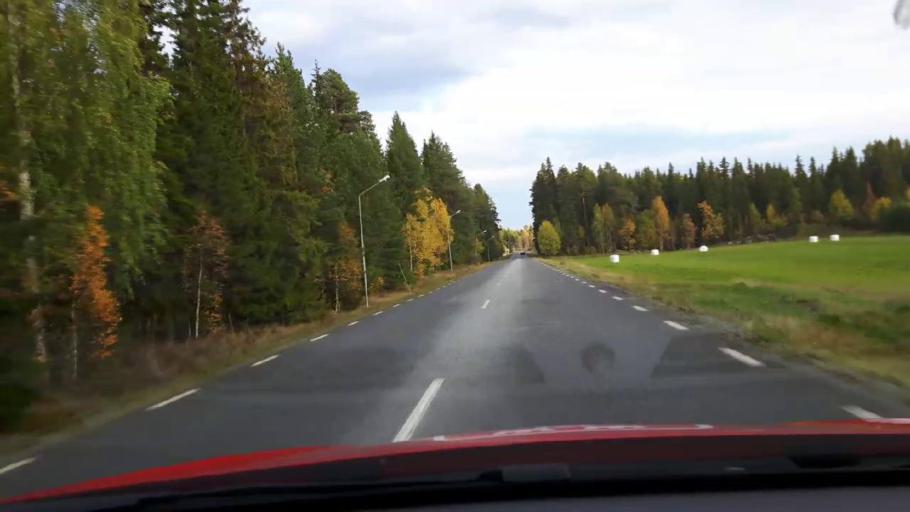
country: SE
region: Jaemtland
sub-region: Krokoms Kommun
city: Krokom
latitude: 63.3503
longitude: 14.5512
